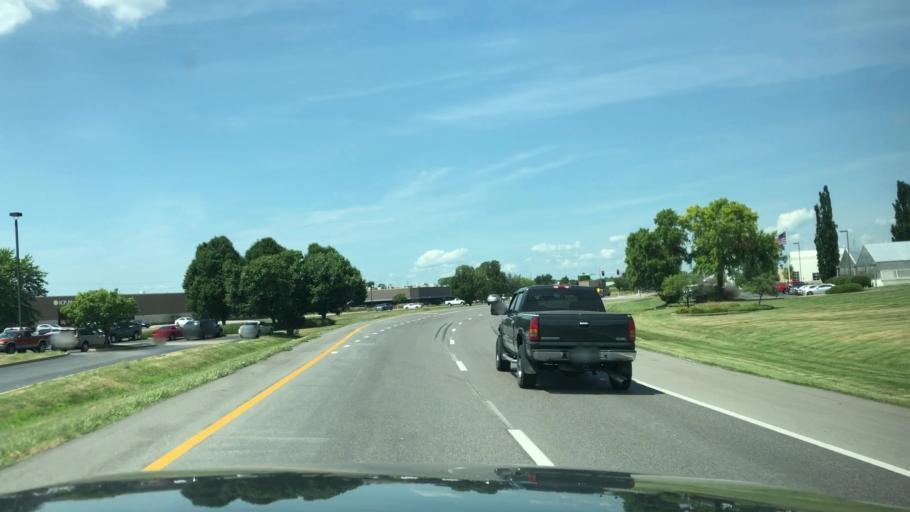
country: US
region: Missouri
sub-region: Saint Charles County
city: Saint Charles
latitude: 38.7742
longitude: -90.4604
